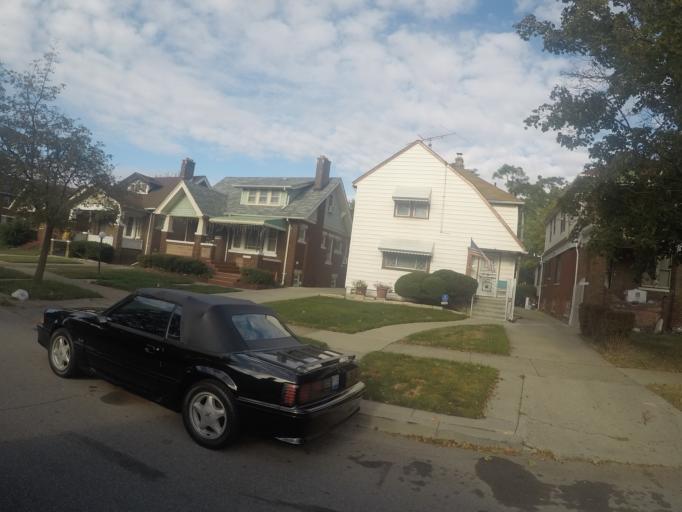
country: US
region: Michigan
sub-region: Wayne County
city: Dearborn
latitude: 42.3640
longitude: -83.1369
